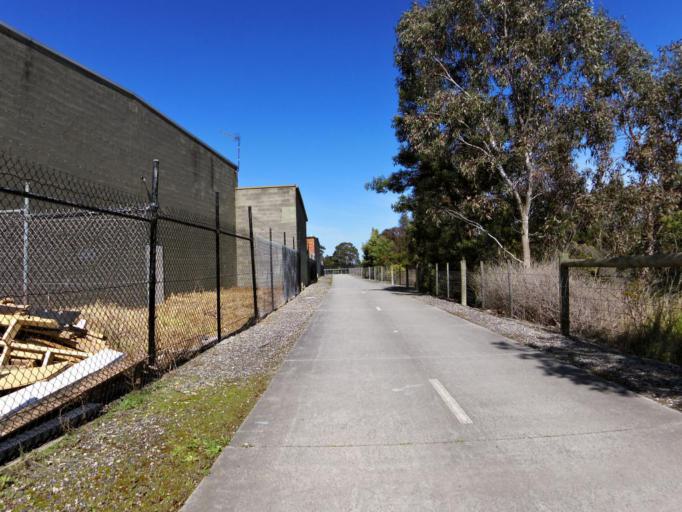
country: AU
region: Victoria
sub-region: Greater Dandenong
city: Dandenong
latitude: -37.9943
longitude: 145.1924
